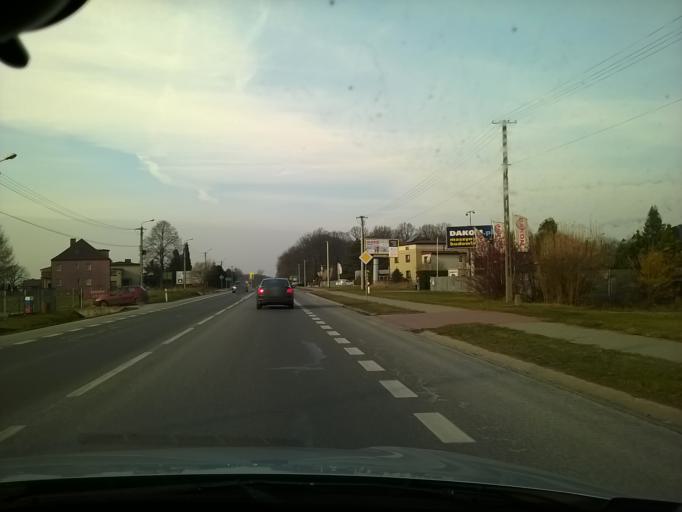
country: PL
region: Silesian Voivodeship
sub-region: Powiat gliwicki
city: Przyszowice
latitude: 50.2418
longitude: 18.7630
